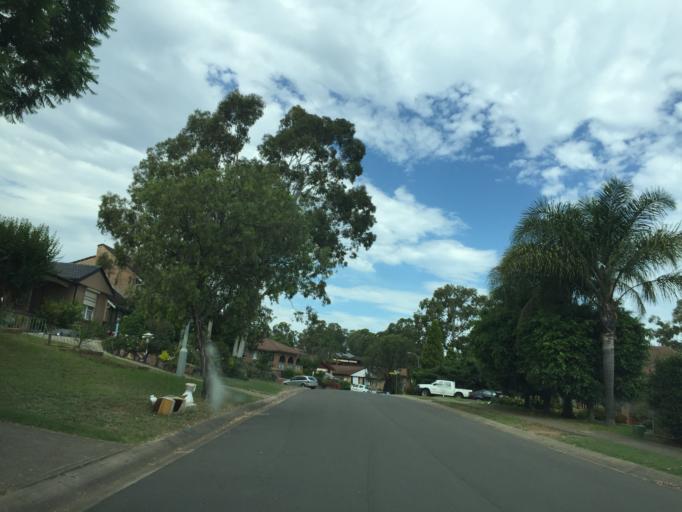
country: AU
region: New South Wales
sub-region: Blacktown
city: Mount Druitt
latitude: -33.7969
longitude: 150.7855
